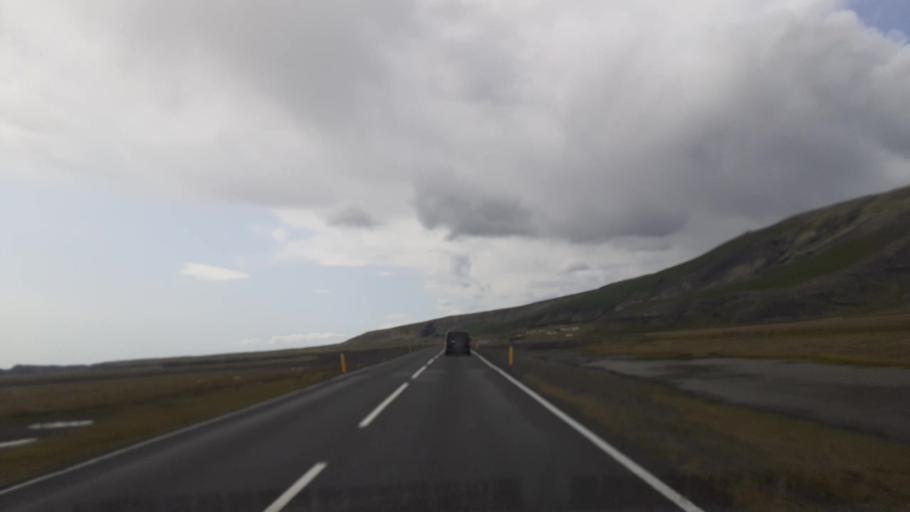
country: IS
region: East
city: Hoefn
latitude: 63.9107
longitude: -16.5509
